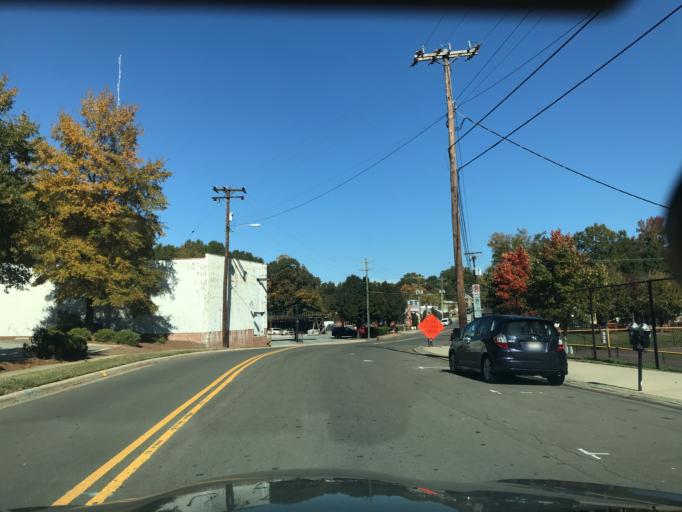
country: US
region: North Carolina
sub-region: Durham County
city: Durham
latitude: 36.0029
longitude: -78.9034
